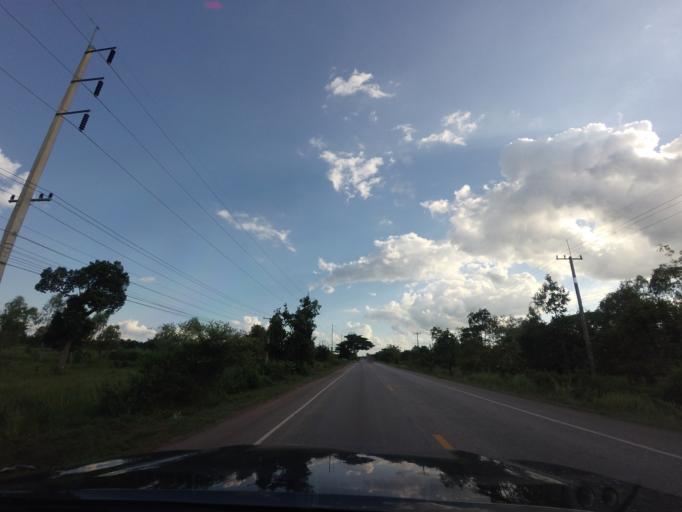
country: TH
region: Changwat Udon Thani
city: Thung Fon
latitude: 17.4752
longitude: 103.1943
